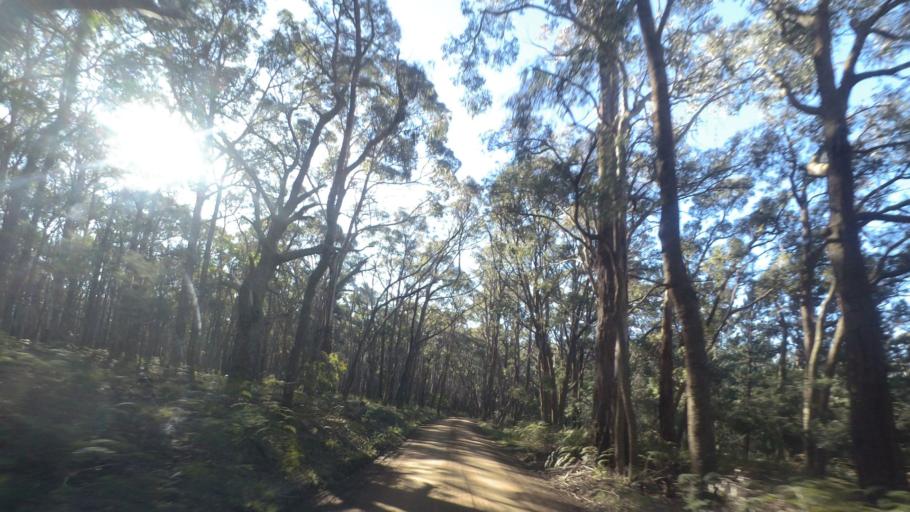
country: AU
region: Victoria
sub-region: Mount Alexander
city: Castlemaine
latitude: -37.2866
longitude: 144.3313
